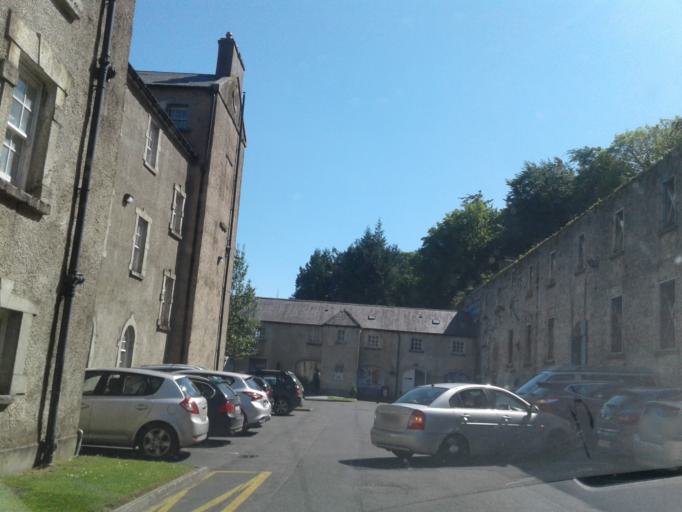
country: IE
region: Leinster
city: Ballinteer
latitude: 53.1994
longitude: -6.2925
